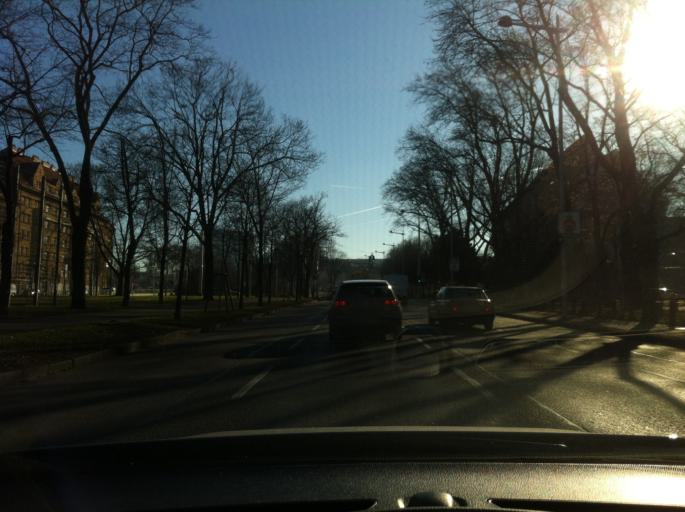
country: AT
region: Vienna
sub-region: Wien Stadt
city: Vienna
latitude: 48.1824
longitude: 16.3469
